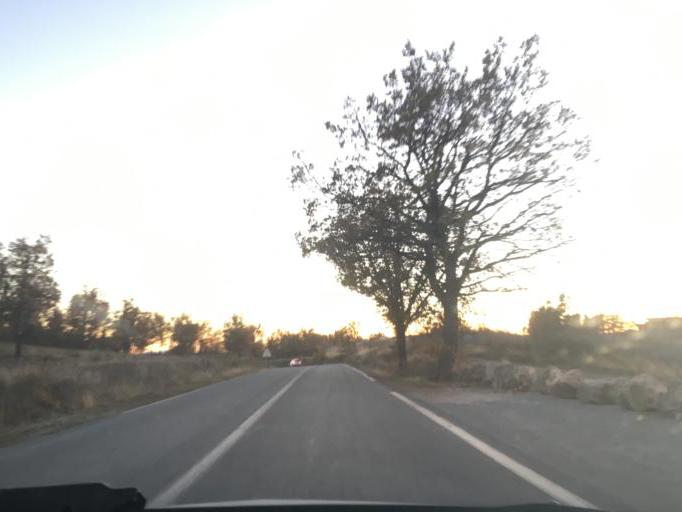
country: FR
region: Provence-Alpes-Cote d'Azur
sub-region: Departement du Var
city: Montferrat
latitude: 43.6484
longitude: 6.4747
